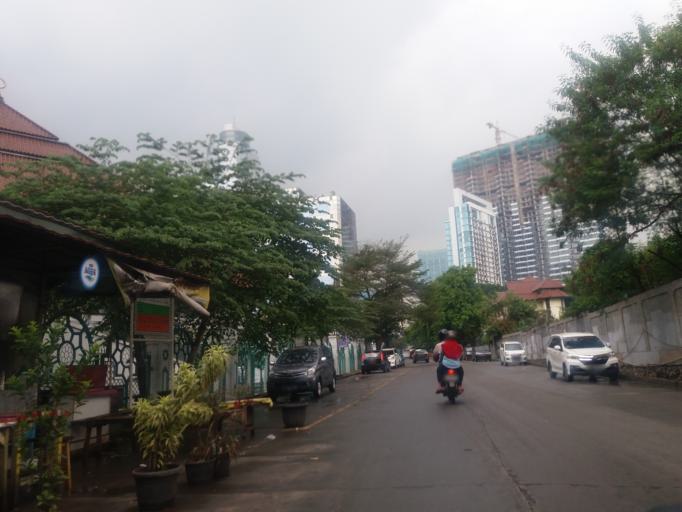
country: ID
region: Jakarta Raya
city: Jakarta
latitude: -6.2194
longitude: 106.8303
